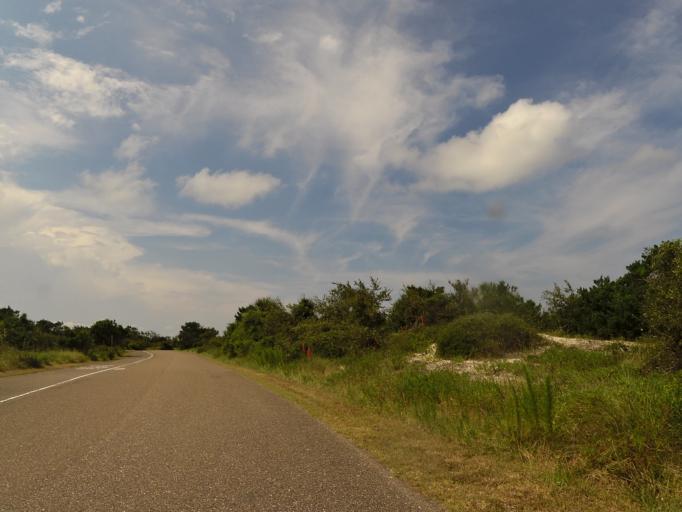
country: US
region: Florida
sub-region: Duval County
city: Atlantic Beach
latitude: 30.4457
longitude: -81.4140
